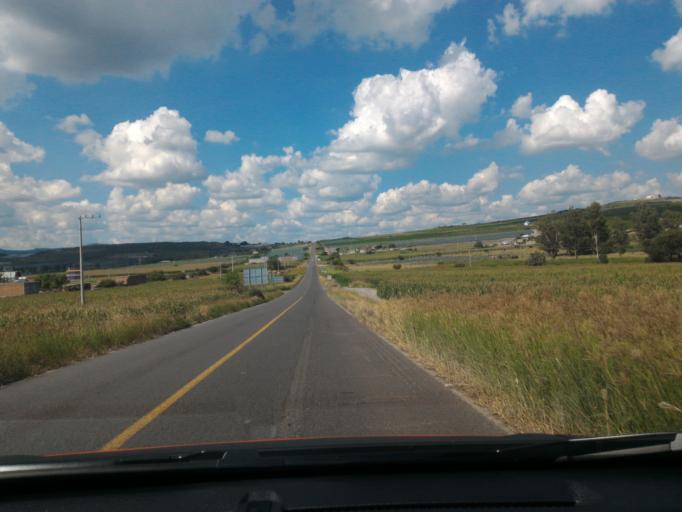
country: MX
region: Guanajuato
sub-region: Penjamo
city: Estacion la Piedad
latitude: 20.4122
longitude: -101.9967
